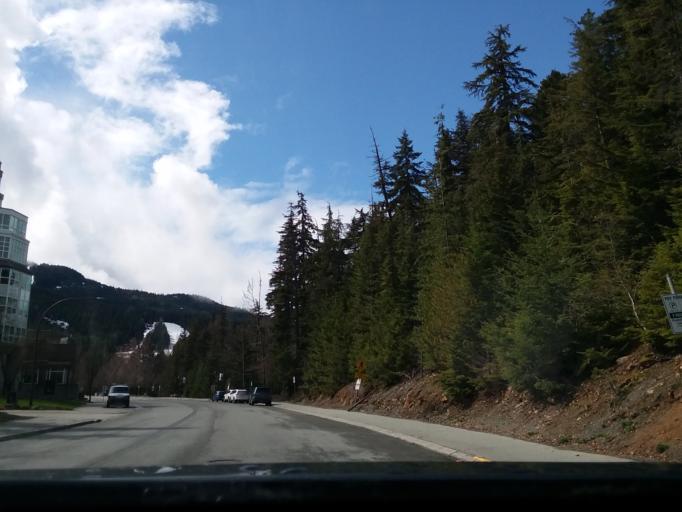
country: CA
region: British Columbia
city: Whistler
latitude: 50.1173
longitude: -122.9482
